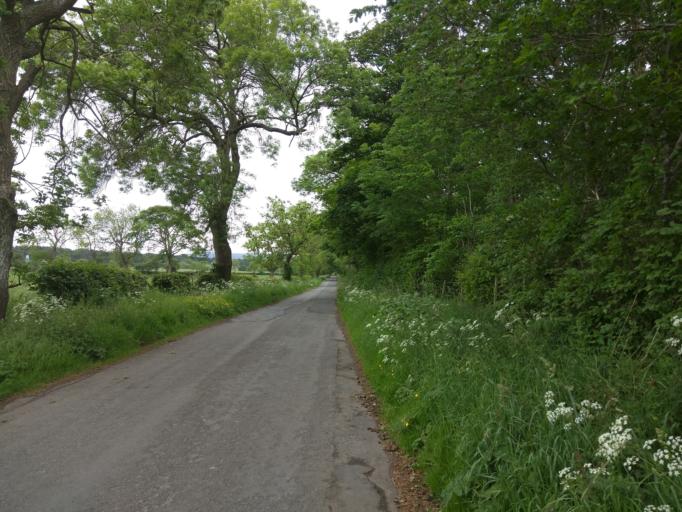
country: GB
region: Scotland
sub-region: Edinburgh
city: Balerno
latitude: 55.8732
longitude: -3.3584
